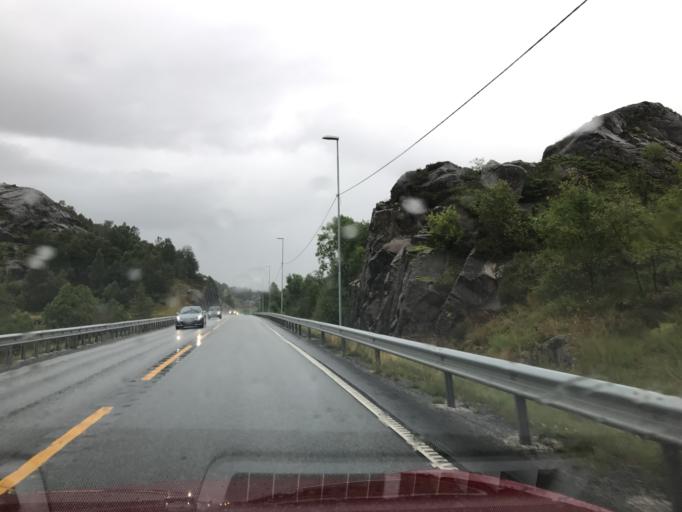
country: NO
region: Rogaland
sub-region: Bjerkreim
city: Vikesa
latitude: 58.5464
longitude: 6.0634
